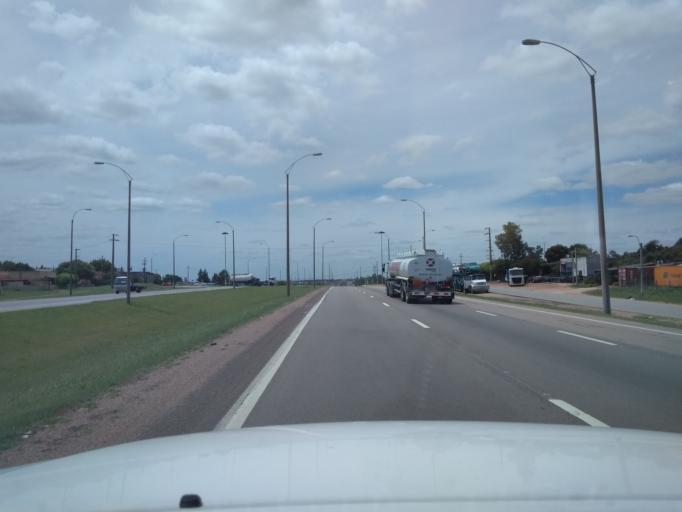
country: UY
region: Canelones
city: La Paz
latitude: -34.7689
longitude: -56.2671
